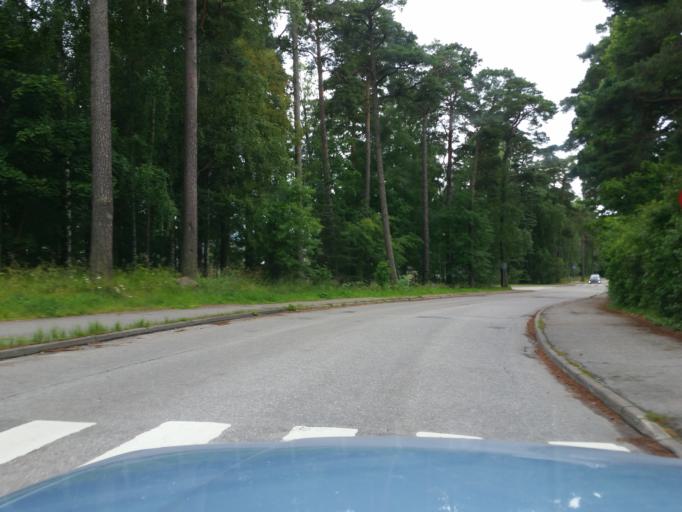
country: FI
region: Uusimaa
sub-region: Raaseporin
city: Hanko
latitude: 59.8292
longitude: 22.9892
